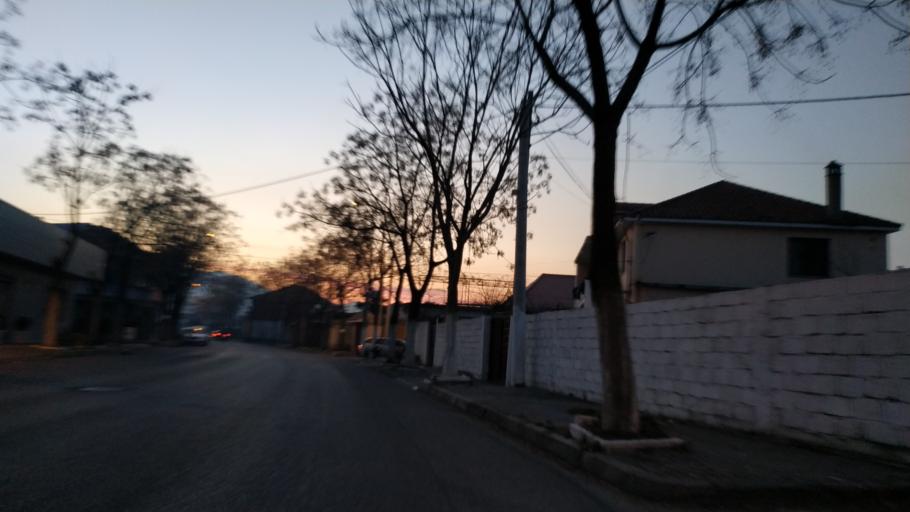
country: AL
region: Shkoder
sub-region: Rrethi i Shkodres
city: Shkoder
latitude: 42.0780
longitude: 19.5061
